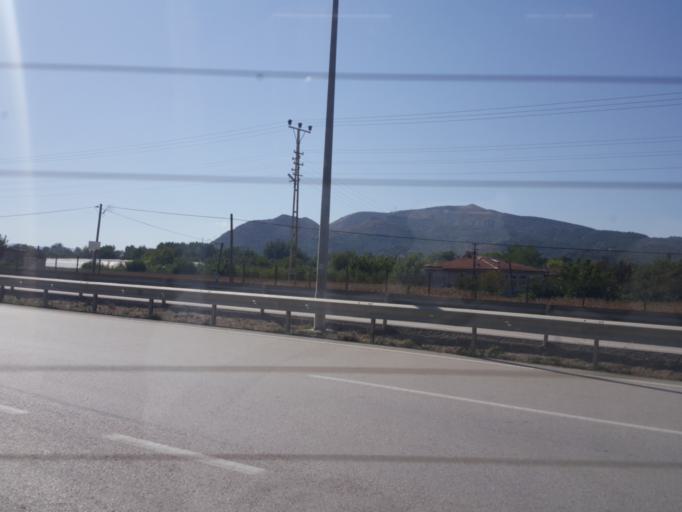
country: TR
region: Amasya
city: Amasya
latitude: 40.6062
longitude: 35.8124
